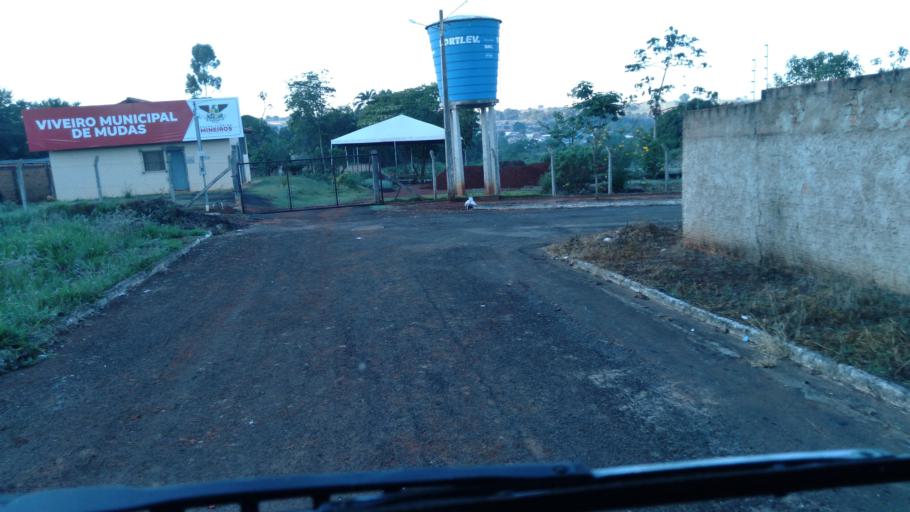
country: BR
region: Goias
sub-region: Mineiros
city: Mineiros
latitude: -17.5764
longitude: -52.5678
